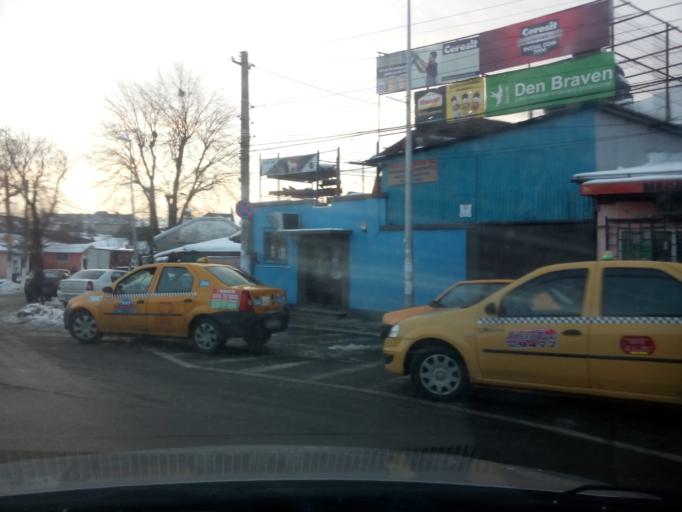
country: RO
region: Ilfov
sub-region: Comuna Pantelimon
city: Pantelimon
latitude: 44.4516
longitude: 26.2051
